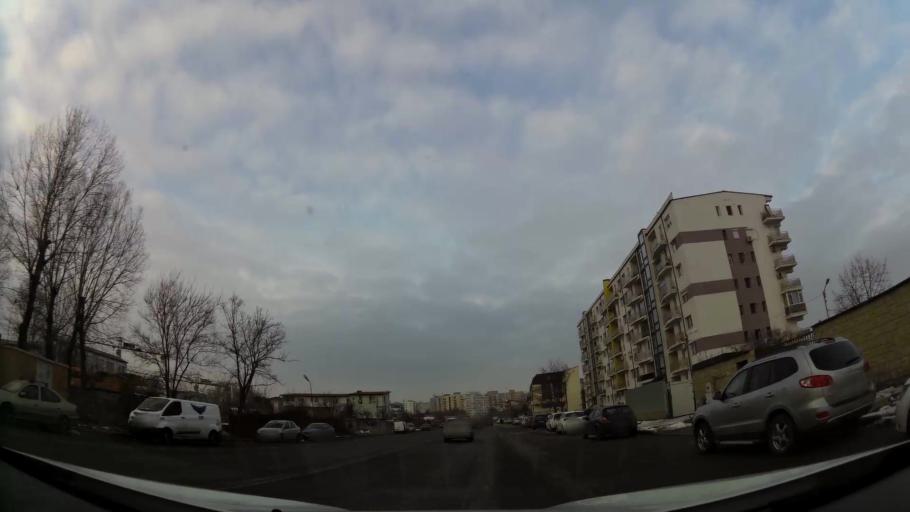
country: RO
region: Ilfov
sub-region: Comuna Fundeni-Dobroesti
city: Fundeni
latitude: 44.4376
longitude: 26.1511
